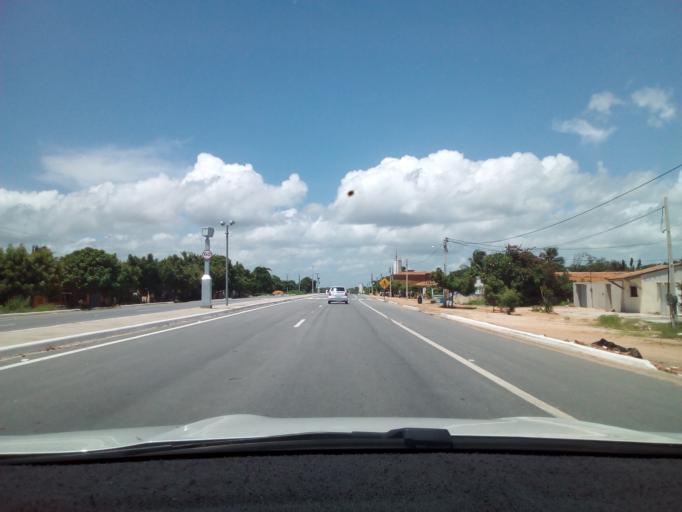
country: BR
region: Ceara
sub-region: Aracati
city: Aracati
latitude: -4.4998
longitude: -37.8003
